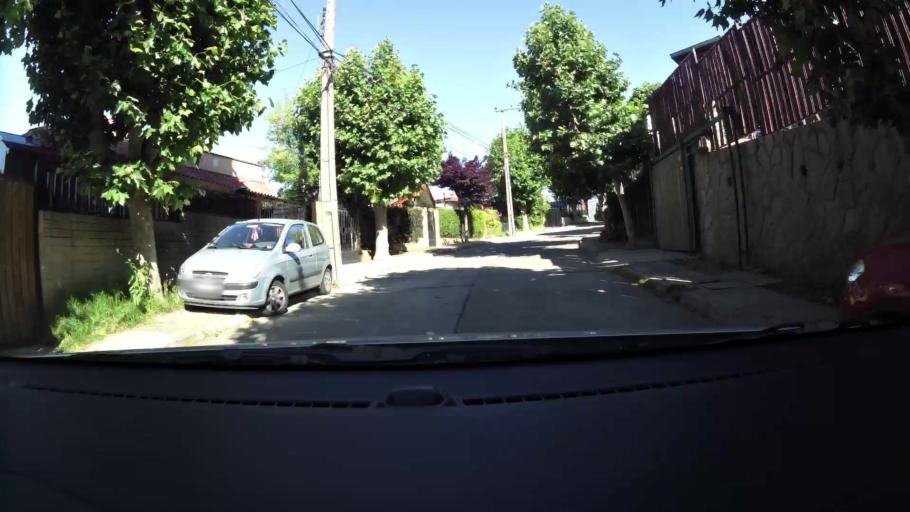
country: CL
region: Valparaiso
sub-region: Provincia de Valparaiso
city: Vina del Mar
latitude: -33.0345
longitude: -71.5555
